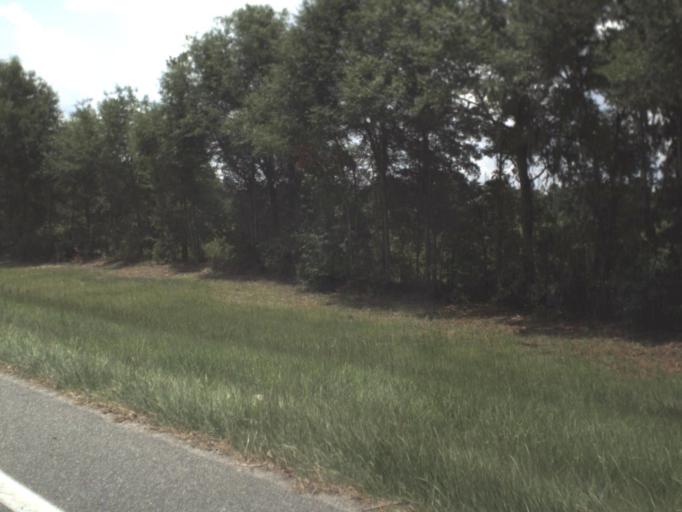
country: US
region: Florida
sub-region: Hamilton County
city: Jasper
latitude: 30.5276
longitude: -83.0341
